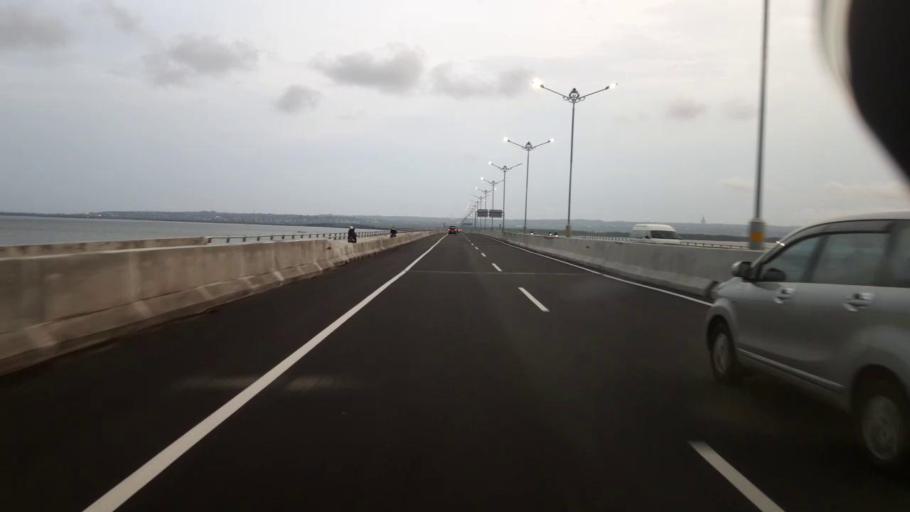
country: ID
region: Bali
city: Kelanabian
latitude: -8.7482
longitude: 115.1958
